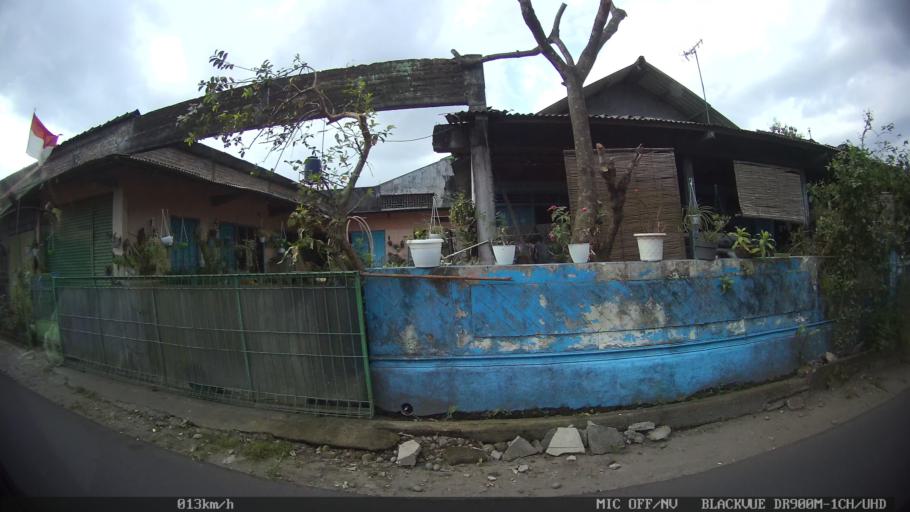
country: ID
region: Daerah Istimewa Yogyakarta
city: Gamping Lor
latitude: -7.7895
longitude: 110.3412
